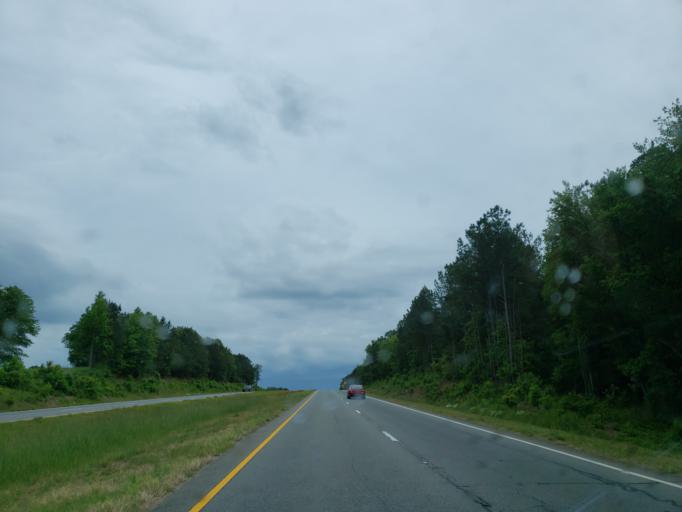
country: US
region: Georgia
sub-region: Haralson County
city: Bremen
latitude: 33.7486
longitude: -85.1607
